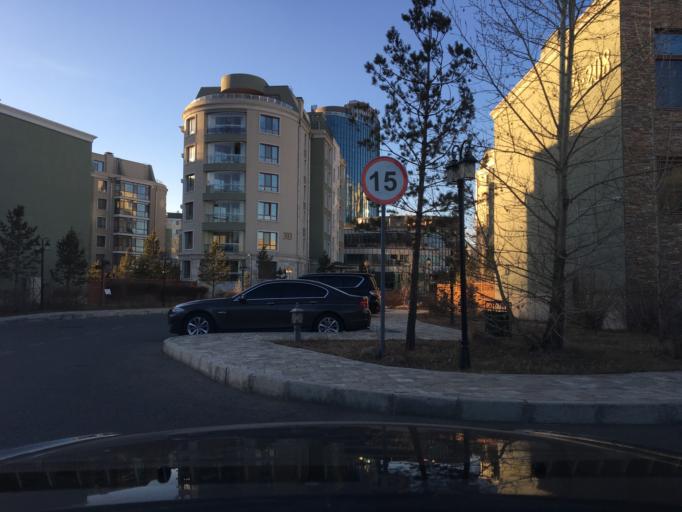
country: MN
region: Ulaanbaatar
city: Ulaanbaatar
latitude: 47.8890
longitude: 106.9344
